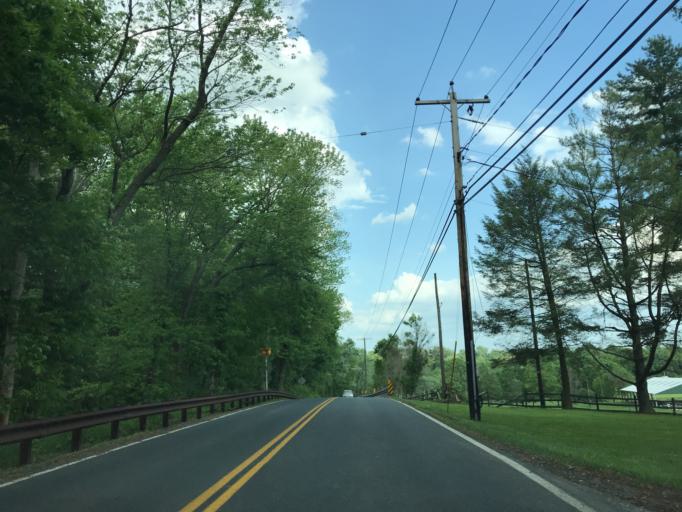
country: US
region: Maryland
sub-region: Harford County
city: North Bel Air
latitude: 39.5282
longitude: -76.3724
